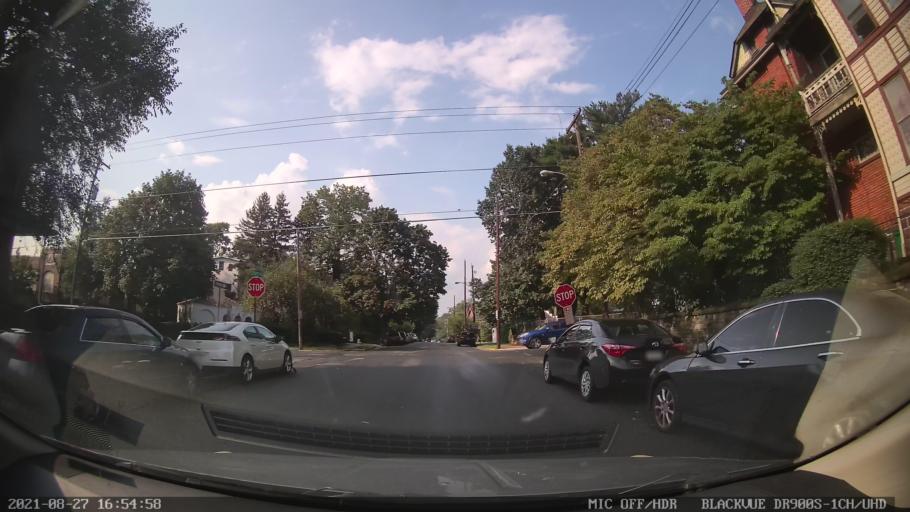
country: US
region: Pennsylvania
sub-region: Berks County
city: Reading
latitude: 40.3459
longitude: -75.9315
